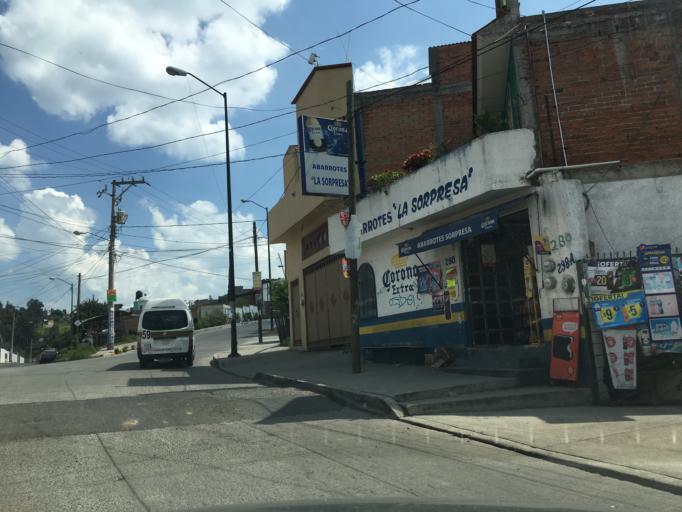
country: MX
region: Michoacan
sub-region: Morelia
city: Montana Monarca (Punta Altozano)
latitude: 19.6686
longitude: -101.1842
